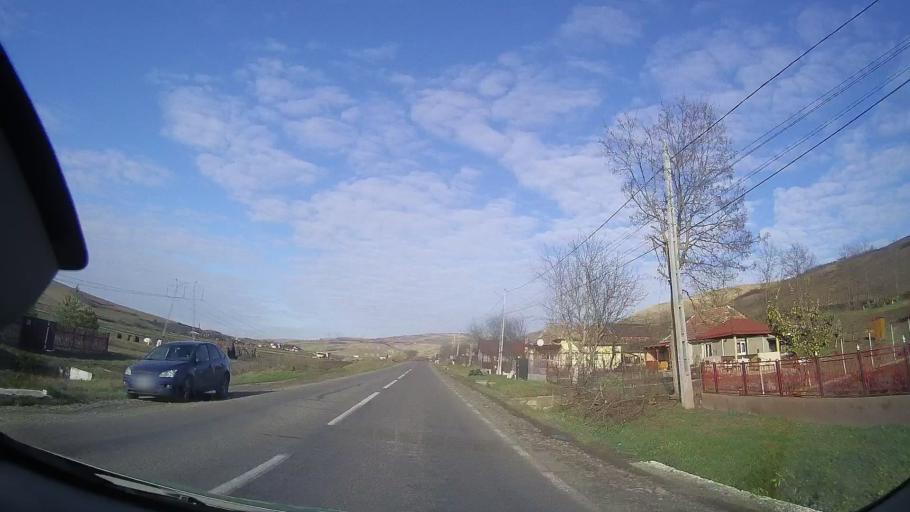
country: RO
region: Cluj
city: Caianu Mic
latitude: 46.8019
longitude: 23.8740
